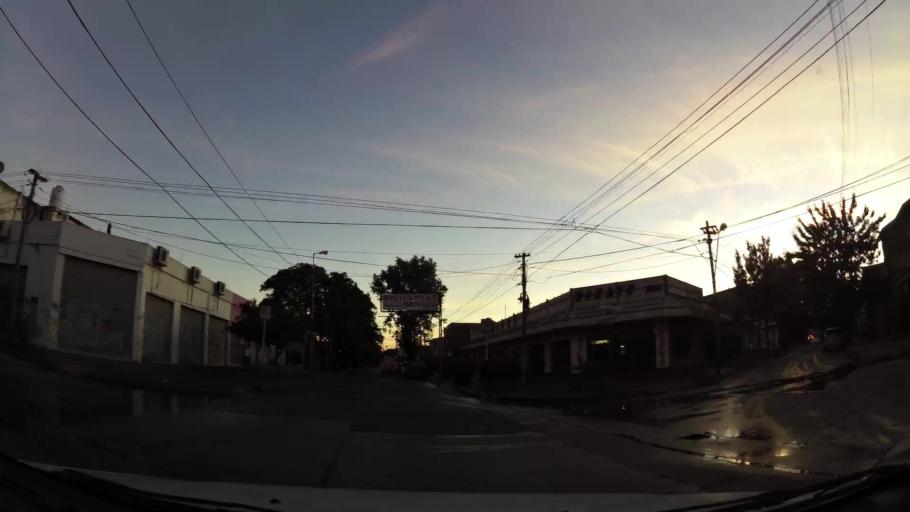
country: AR
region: Buenos Aires
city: Ituzaingo
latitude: -34.6562
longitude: -58.6437
